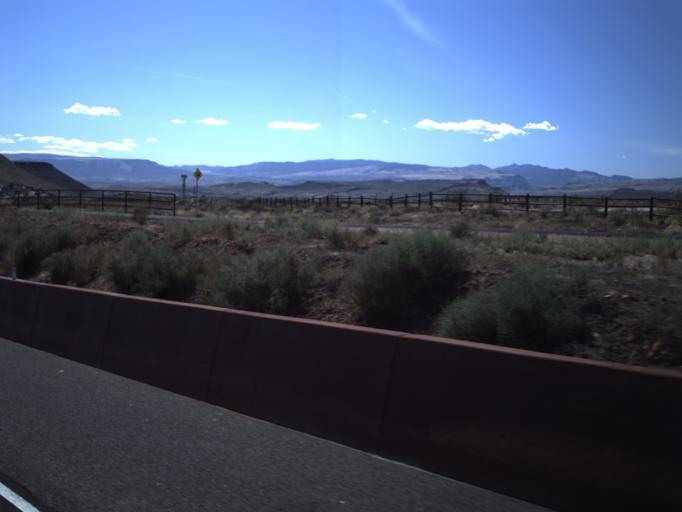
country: US
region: Utah
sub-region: Washington County
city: Saint George
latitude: 37.1385
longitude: -113.6037
